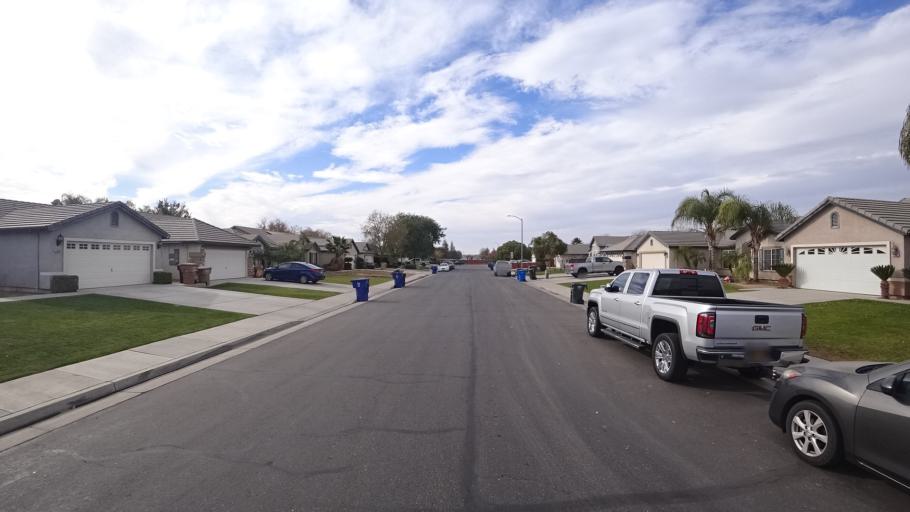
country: US
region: California
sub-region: Kern County
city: Rosedale
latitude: 35.4191
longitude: -119.1391
